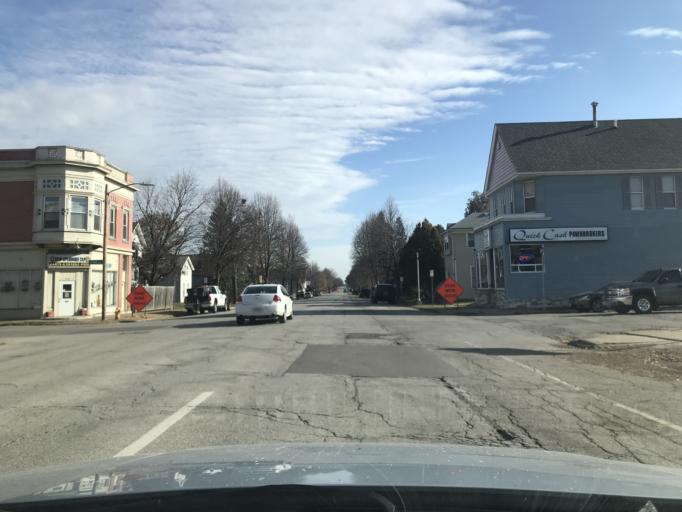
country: US
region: Iowa
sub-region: Scott County
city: Davenport
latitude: 41.5223
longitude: -90.6116
